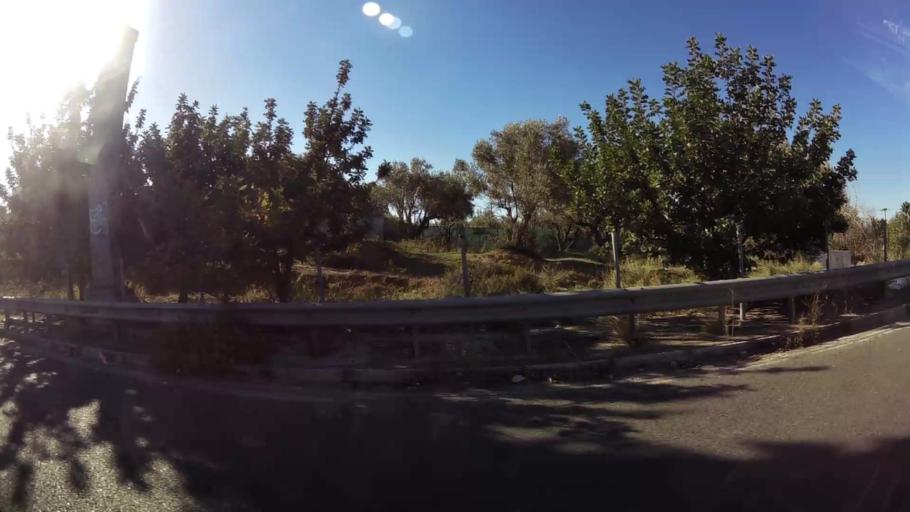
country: GR
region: Attica
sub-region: Nomarchia Athinas
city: Lykovrysi
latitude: 38.0963
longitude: 23.7738
